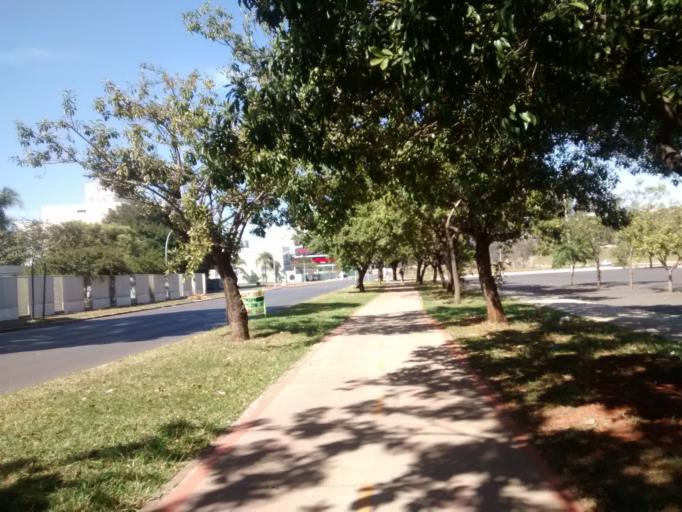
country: BR
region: Federal District
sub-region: Brasilia
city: Brasilia
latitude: -15.7801
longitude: -47.8908
